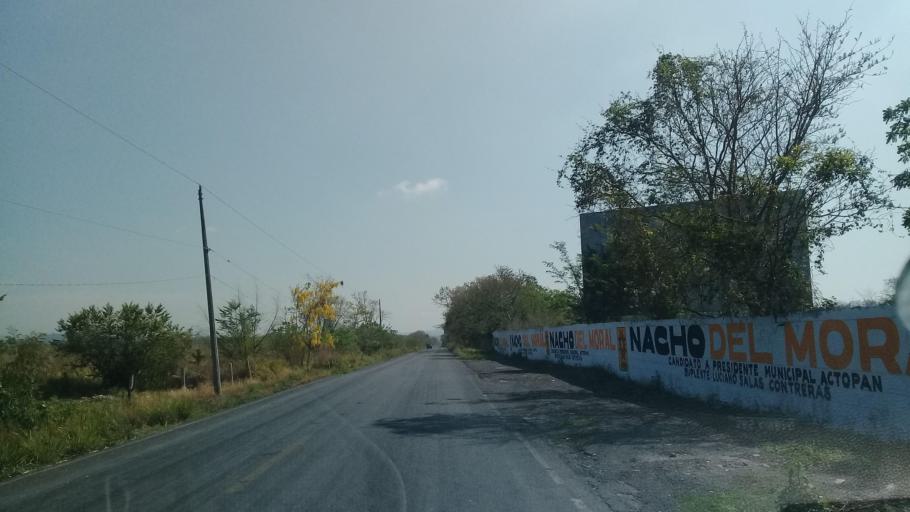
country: MX
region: Veracruz
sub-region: Emiliano Zapata
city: Plan del Rio
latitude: 19.3986
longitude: -96.6165
